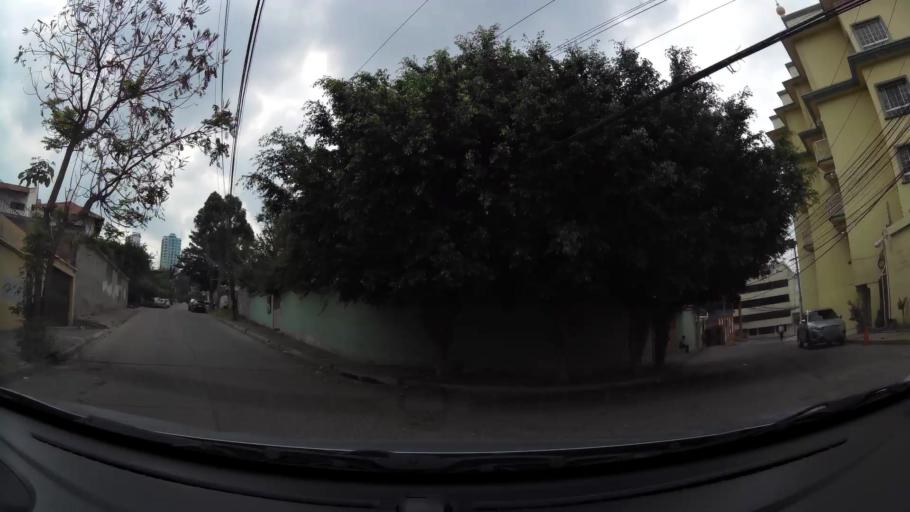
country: HN
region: Francisco Morazan
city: Tegucigalpa
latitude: 14.0913
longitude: -87.1929
